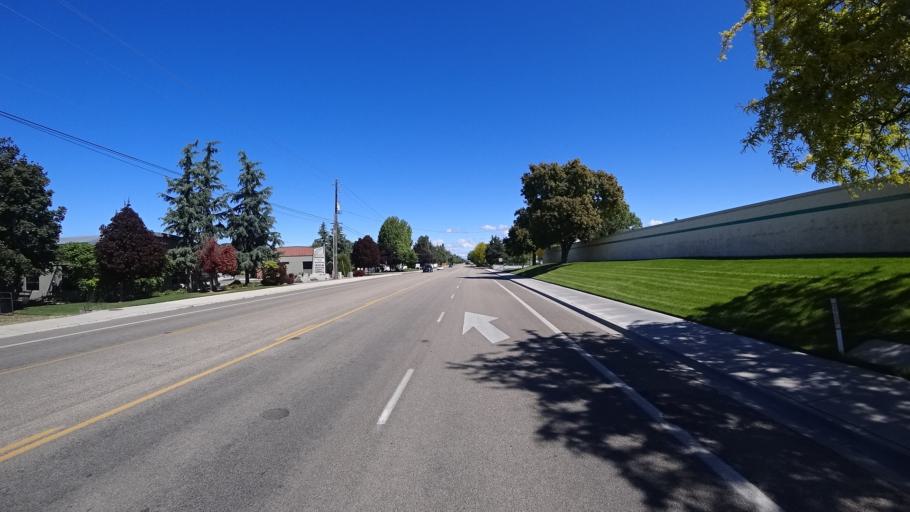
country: US
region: Idaho
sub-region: Ada County
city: Meridian
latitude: 43.6224
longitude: -116.3745
